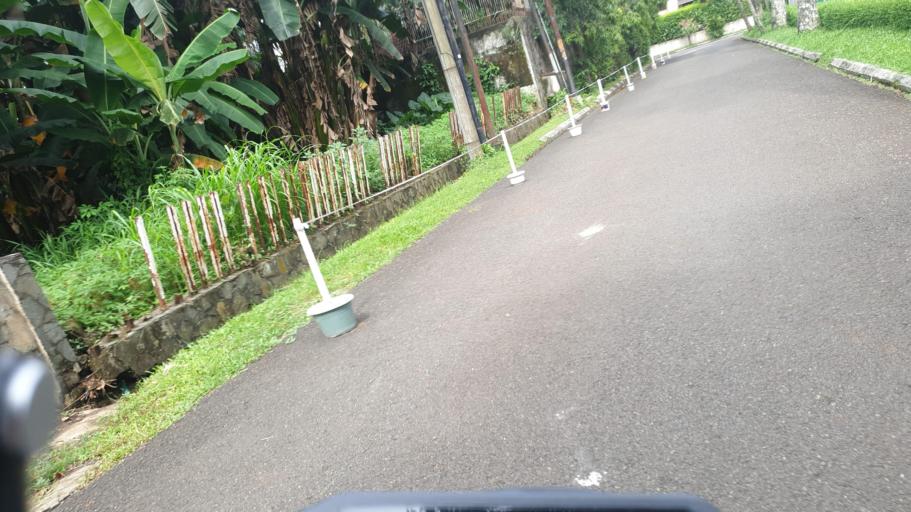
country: ID
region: West Java
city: Pamulang
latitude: -6.2943
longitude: 106.7911
